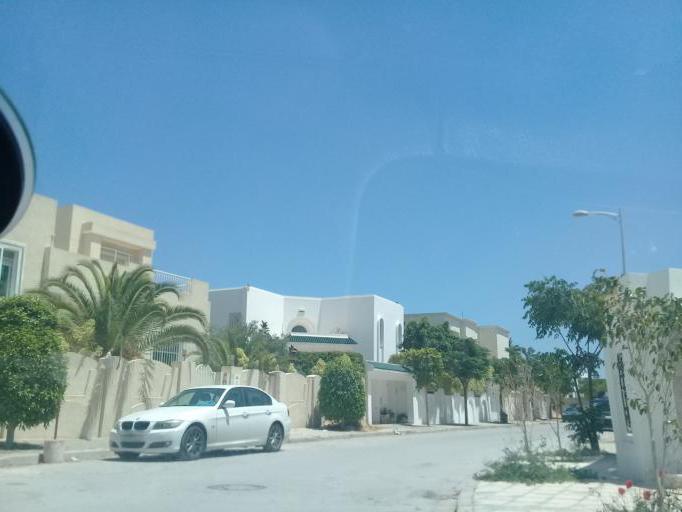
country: TN
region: Tunis
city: La Goulette
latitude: 36.8440
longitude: 10.2666
